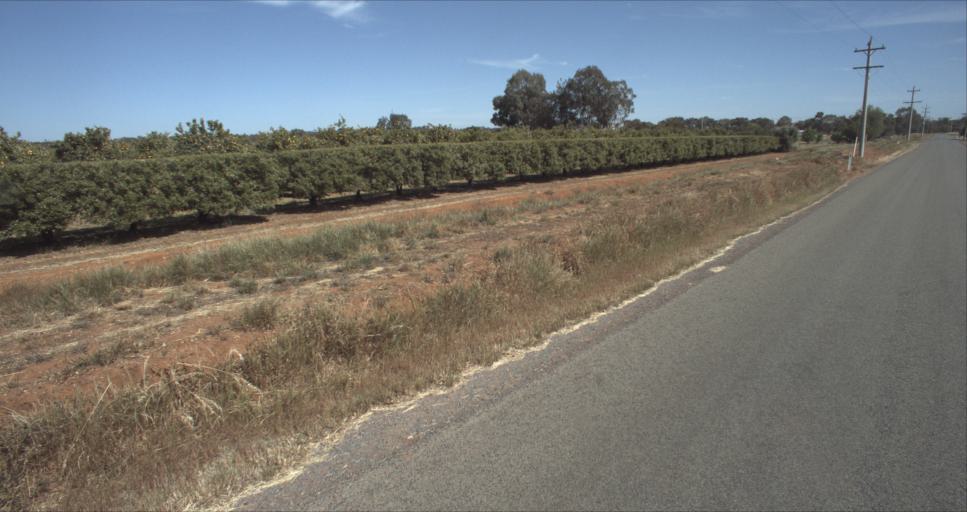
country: AU
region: New South Wales
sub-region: Leeton
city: Leeton
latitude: -34.5819
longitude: 146.4699
